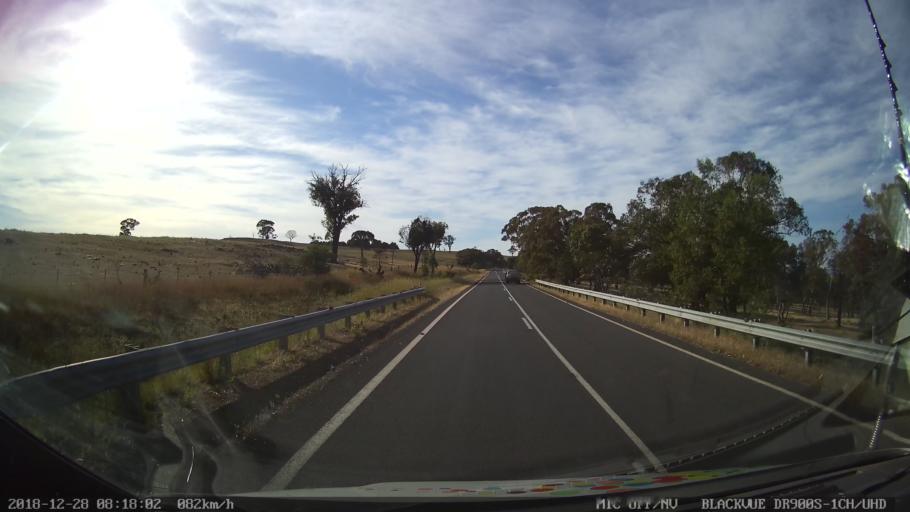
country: AU
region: New South Wales
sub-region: Blayney
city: Blayney
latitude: -33.8427
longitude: 149.3464
